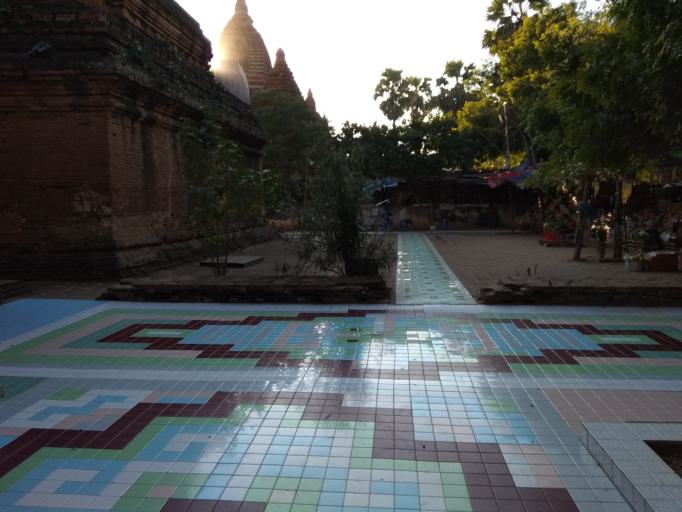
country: MM
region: Magway
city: Chauk
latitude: 21.1575
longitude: 94.8613
